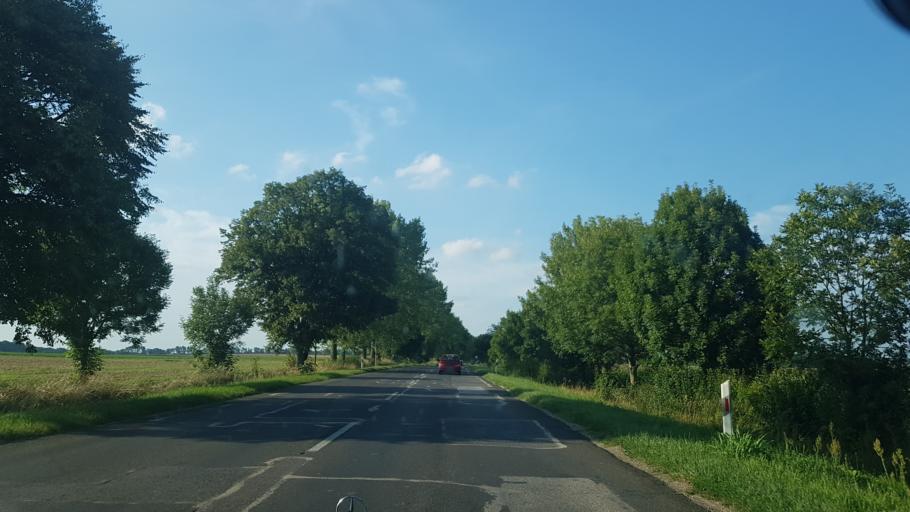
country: HU
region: Somogy
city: Nagyatad
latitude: 46.2496
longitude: 17.3558
